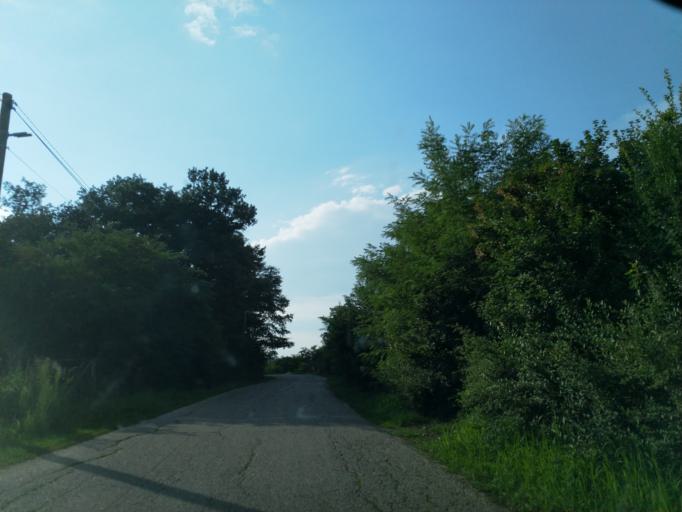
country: RS
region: Central Serbia
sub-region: Pomoravski Okrug
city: Jagodina
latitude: 43.9876
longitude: 21.2129
